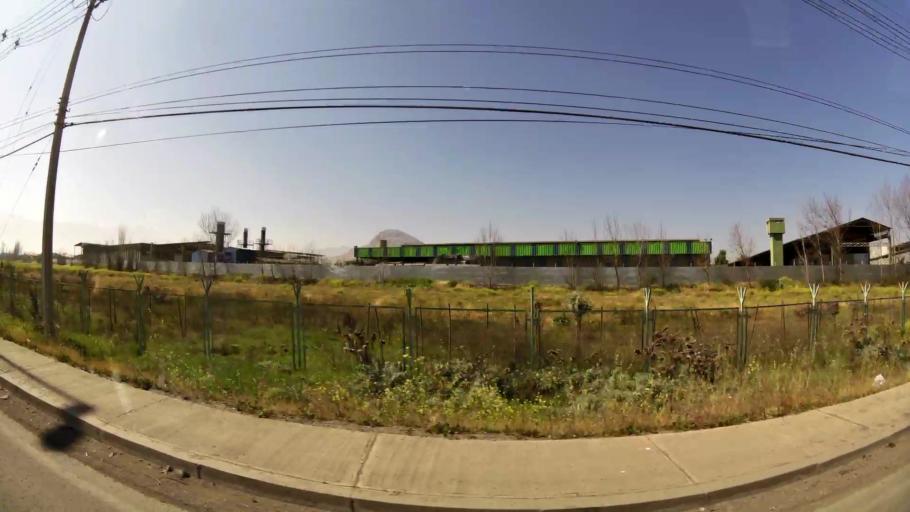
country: CL
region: Santiago Metropolitan
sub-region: Provincia de Chacabuco
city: Chicureo Abajo
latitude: -33.3002
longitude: -70.7280
